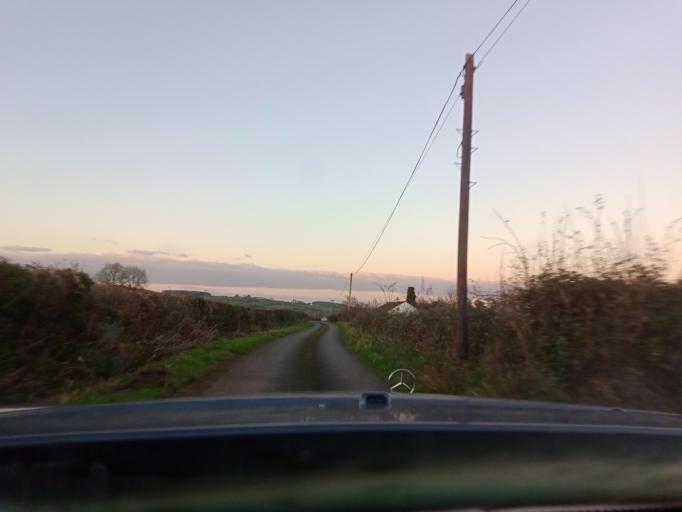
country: IE
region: Leinster
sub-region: Kilkenny
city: Graiguenamanagh
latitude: 52.5618
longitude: -6.9611
